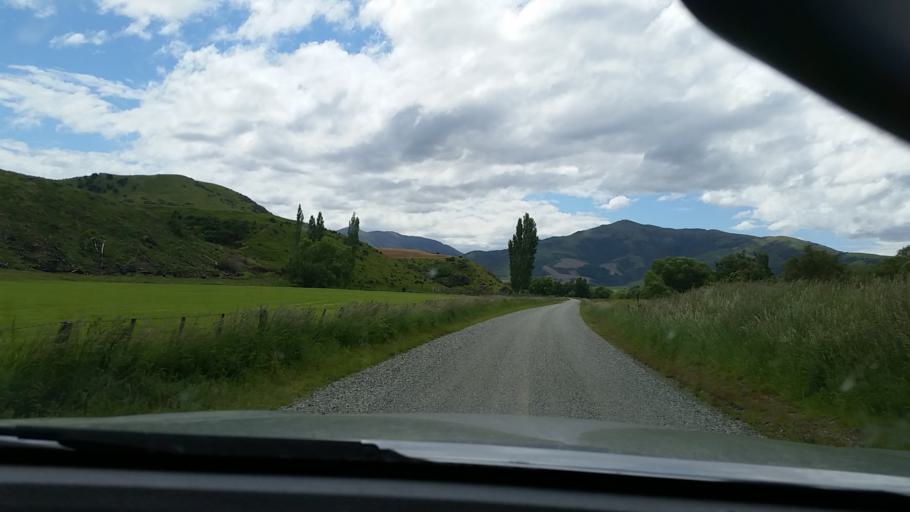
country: NZ
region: Otago
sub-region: Queenstown-Lakes District
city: Kingston
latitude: -45.7241
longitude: 168.6684
